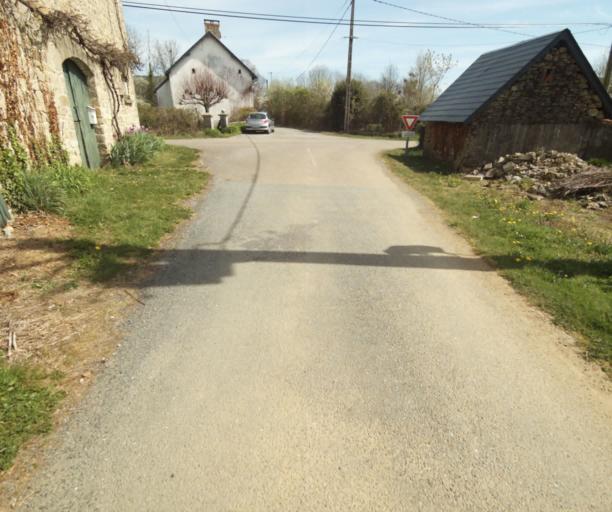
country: FR
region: Limousin
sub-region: Departement de la Correze
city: Naves
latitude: 45.3709
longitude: 1.8016
